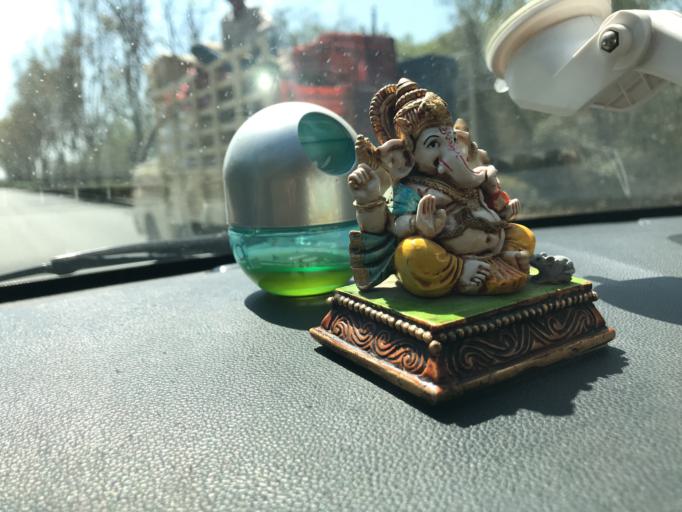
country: IN
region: Telangana
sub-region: Medak
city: Serilingampalle
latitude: 17.4649
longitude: 78.3340
